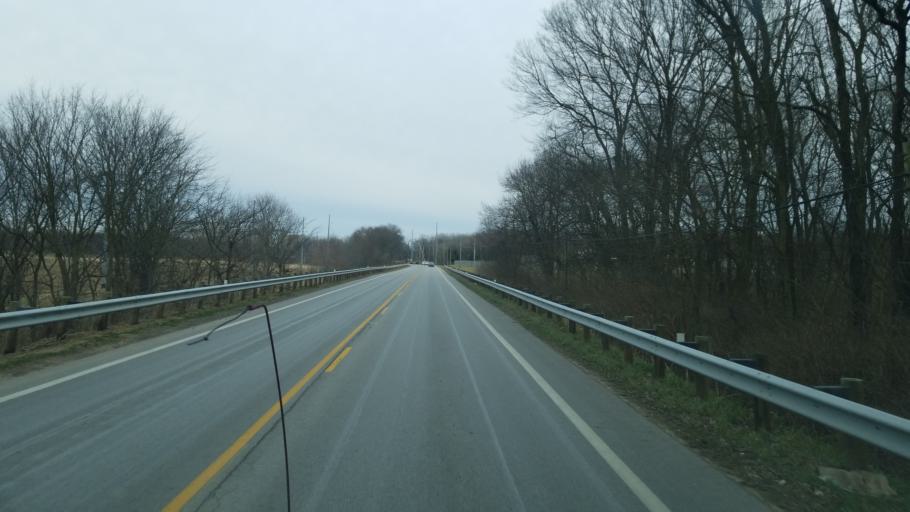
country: US
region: Ohio
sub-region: Pickaway County
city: Circleville
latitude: 39.6011
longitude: -82.9644
